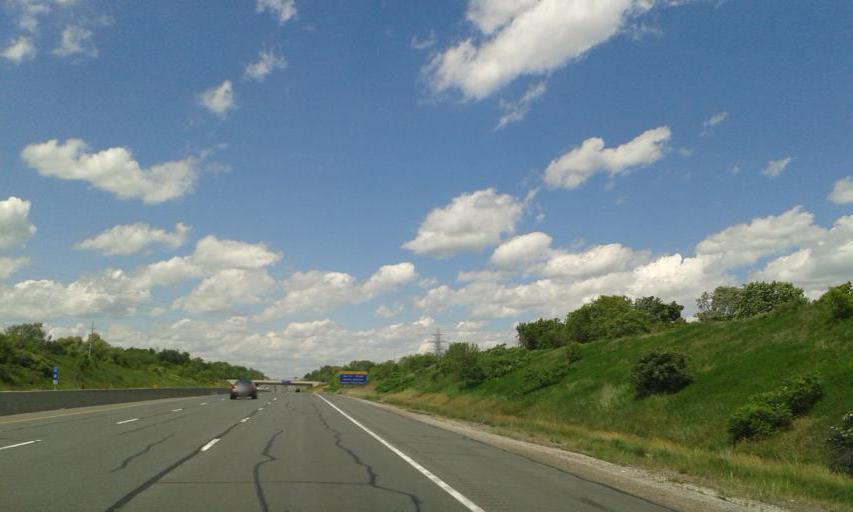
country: CA
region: Ontario
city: Burlington
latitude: 43.3520
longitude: -79.8312
